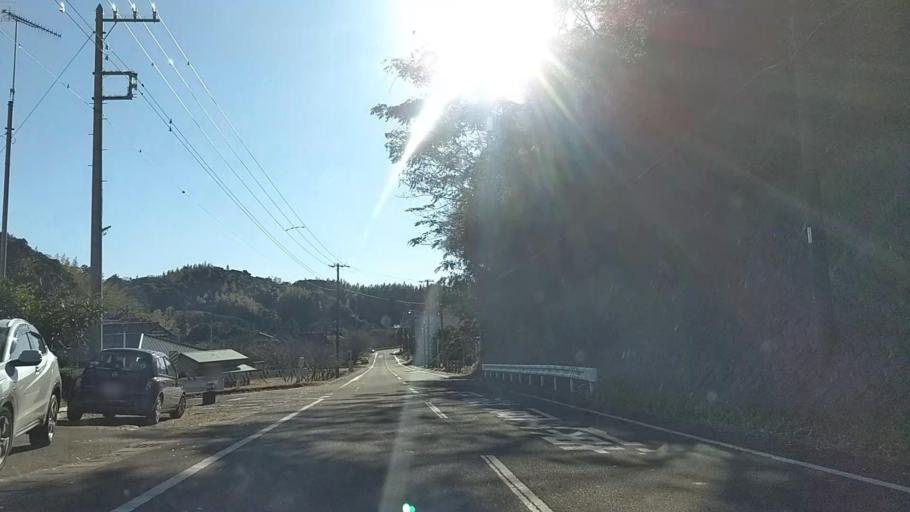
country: JP
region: Chiba
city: Futtsu
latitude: 35.2428
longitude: 139.8727
